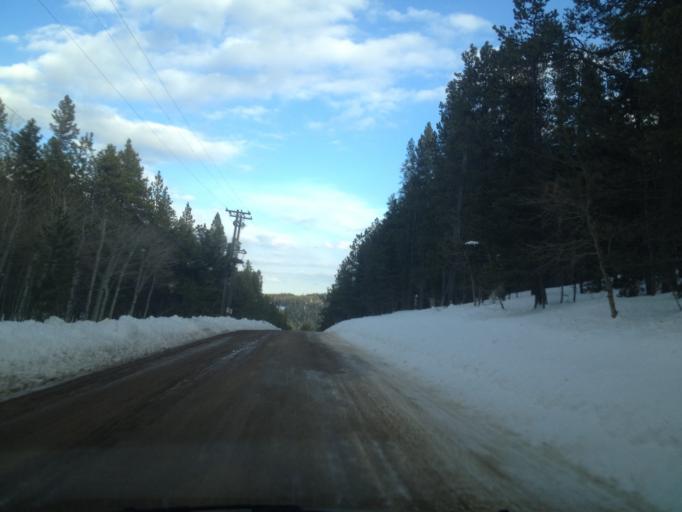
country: US
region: Colorado
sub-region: Boulder County
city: Nederland
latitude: 40.1244
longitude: -105.4592
